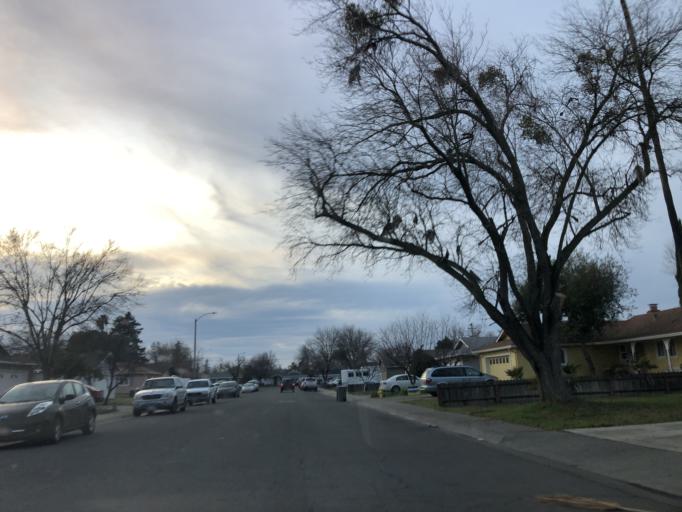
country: US
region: California
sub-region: Yolo County
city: Woodland
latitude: 38.6690
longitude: -121.7589
